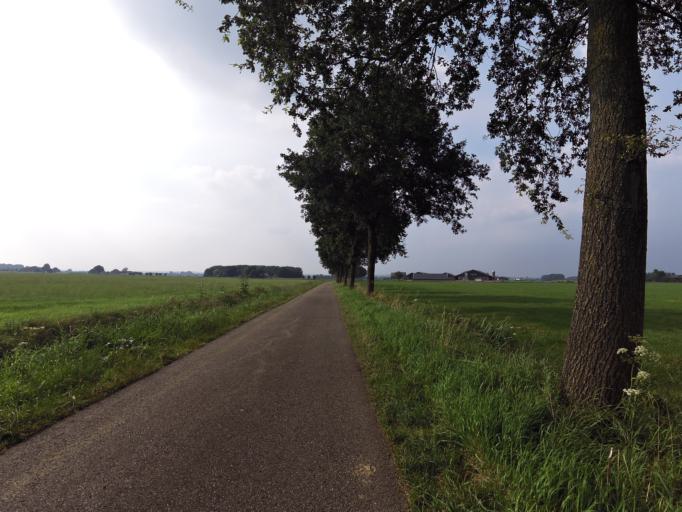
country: NL
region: Gelderland
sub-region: Gemeente Zevenaar
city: Zevenaar
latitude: 51.9722
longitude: 6.0694
